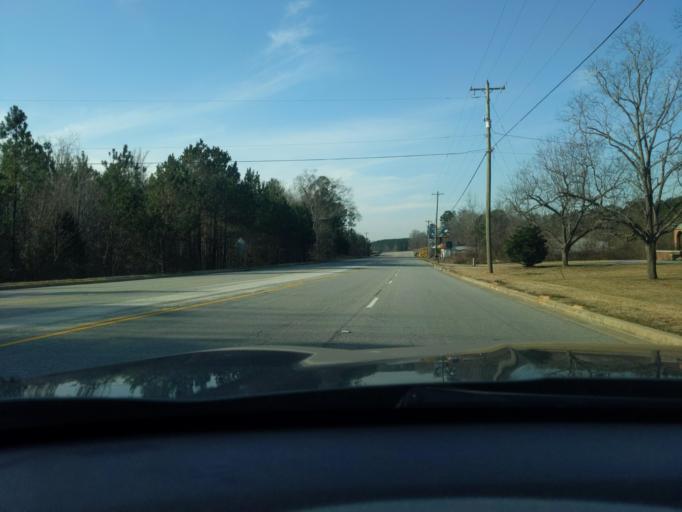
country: US
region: South Carolina
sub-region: Abbeville County
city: Abbeville
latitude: 34.1513
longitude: -82.3963
